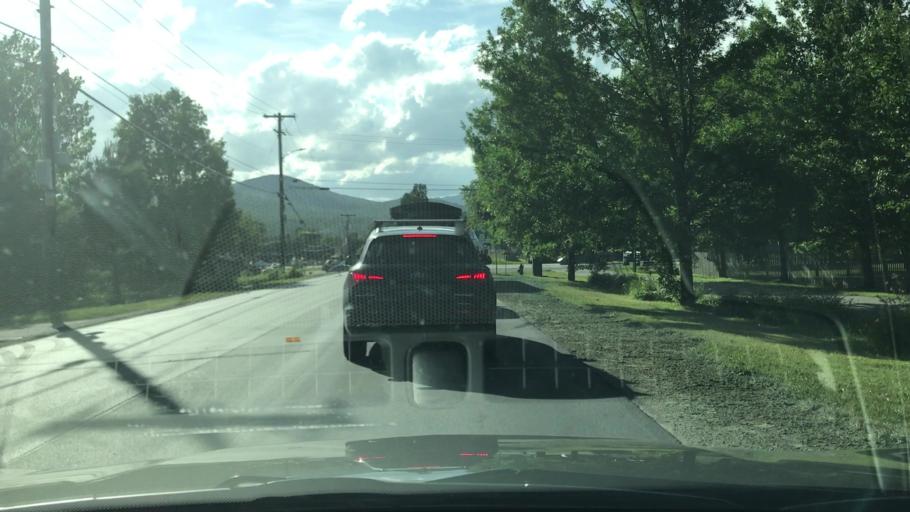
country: US
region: Vermont
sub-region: Lamoille County
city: Morristown
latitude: 44.4726
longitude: -72.7099
